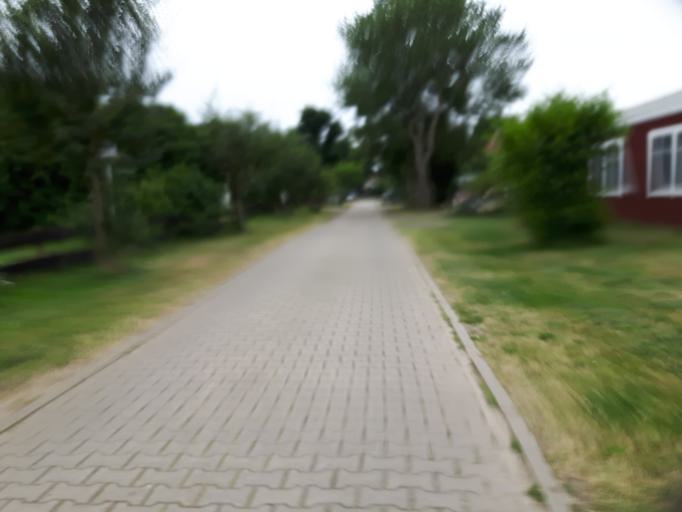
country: DE
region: Lower Saxony
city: Winsen
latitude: 53.3442
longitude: 10.1919
